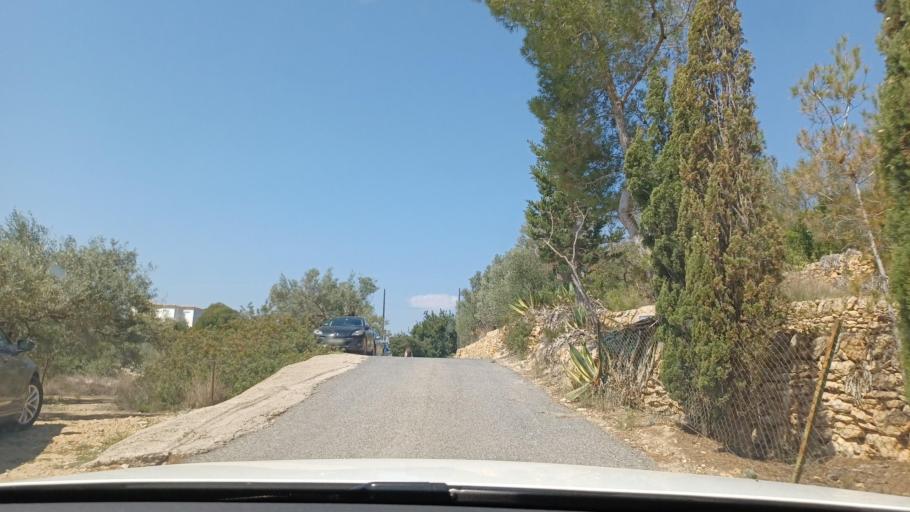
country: ES
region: Catalonia
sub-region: Provincia de Tarragona
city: L'Ampolla
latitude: 40.8281
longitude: 0.7408
